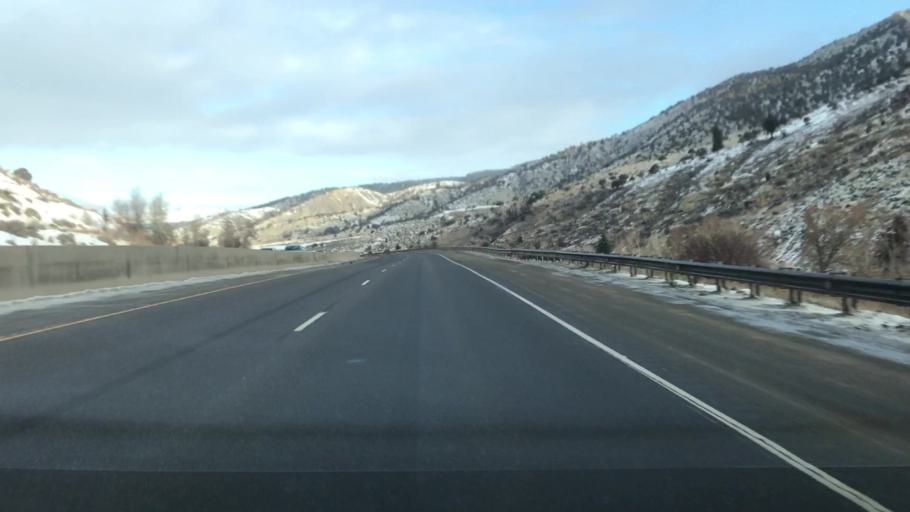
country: US
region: Colorado
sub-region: Eagle County
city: Edwards
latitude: 39.6775
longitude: -106.6479
